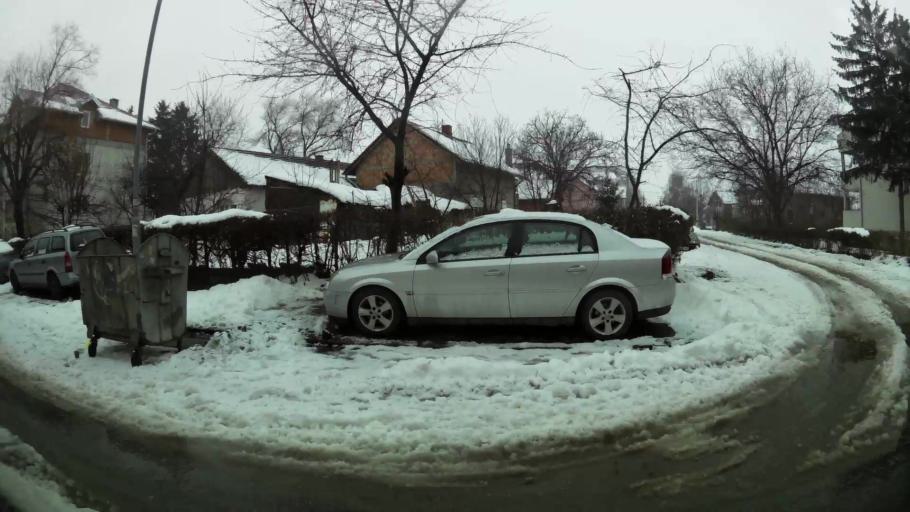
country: RS
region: Central Serbia
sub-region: Belgrade
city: Zemun
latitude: 44.8734
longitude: 20.3186
